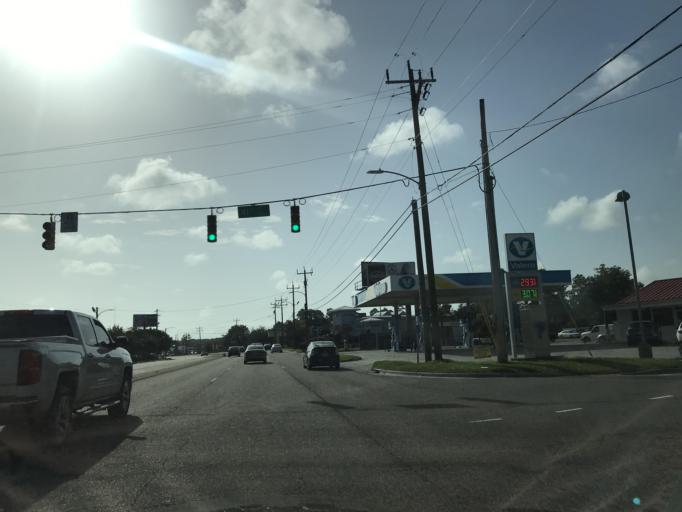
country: US
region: North Carolina
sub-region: New Hanover County
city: Wilmington
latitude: 34.2119
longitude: -77.8955
